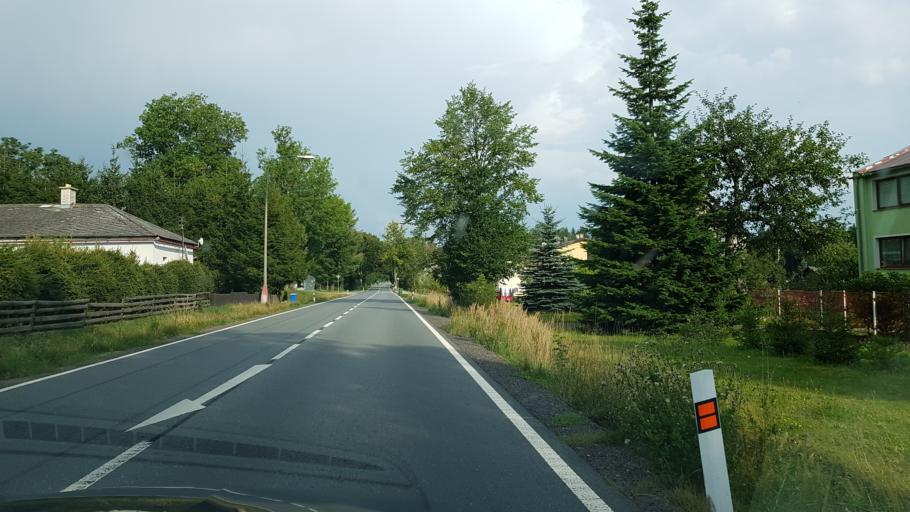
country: CZ
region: Pardubicky
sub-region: Okres Usti nad Orlici
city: Kraliky
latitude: 50.0891
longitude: 16.7192
